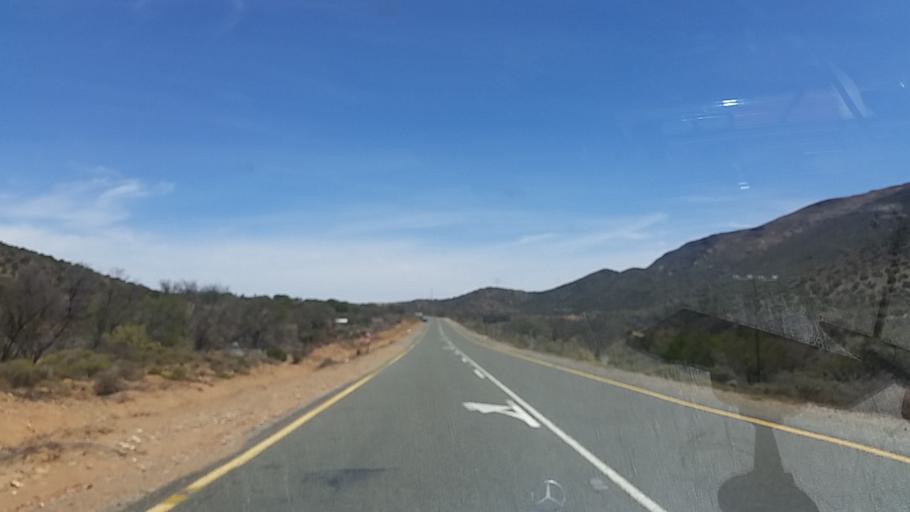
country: ZA
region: Eastern Cape
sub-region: Cacadu District Municipality
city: Willowmore
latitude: -33.4102
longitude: 23.3264
